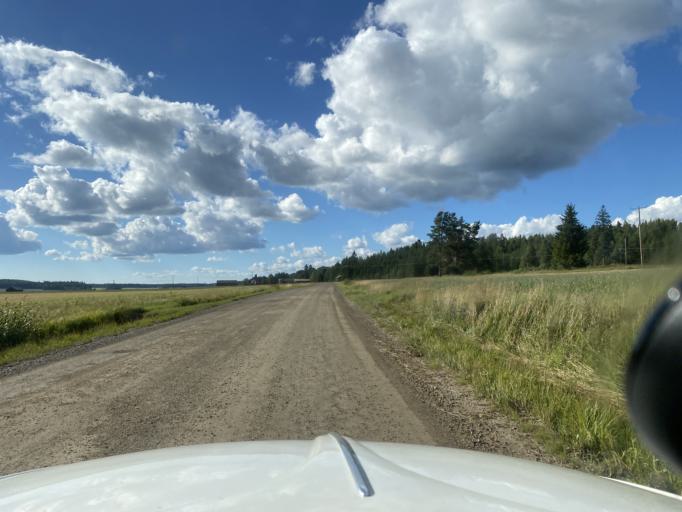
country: FI
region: Pirkanmaa
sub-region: Lounais-Pirkanmaa
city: Punkalaidun
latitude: 61.1420
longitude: 23.2043
